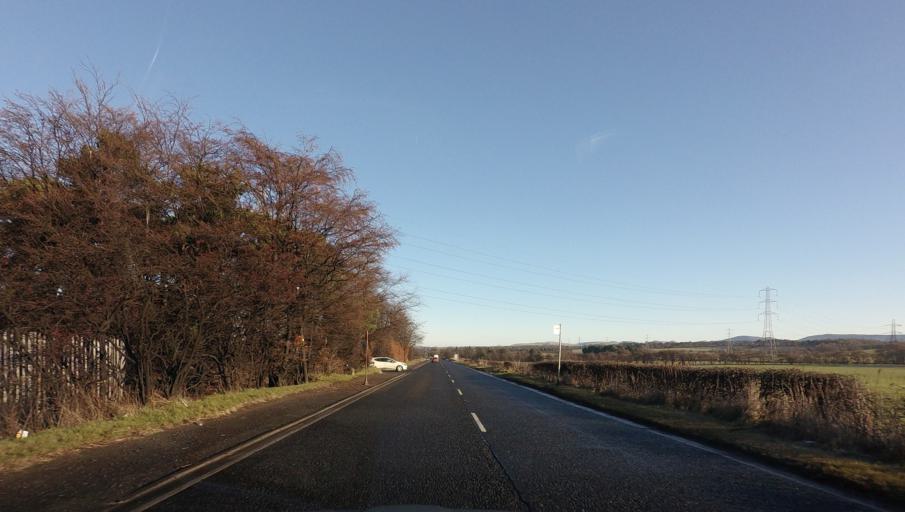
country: GB
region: Scotland
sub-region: West Lothian
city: West Calder
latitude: 55.8408
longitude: -3.6045
